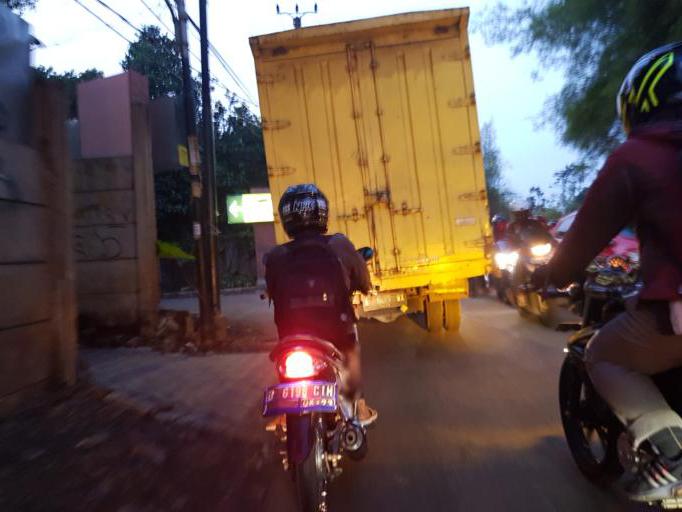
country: ID
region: West Java
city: Serpong
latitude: -6.3305
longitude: 106.6856
